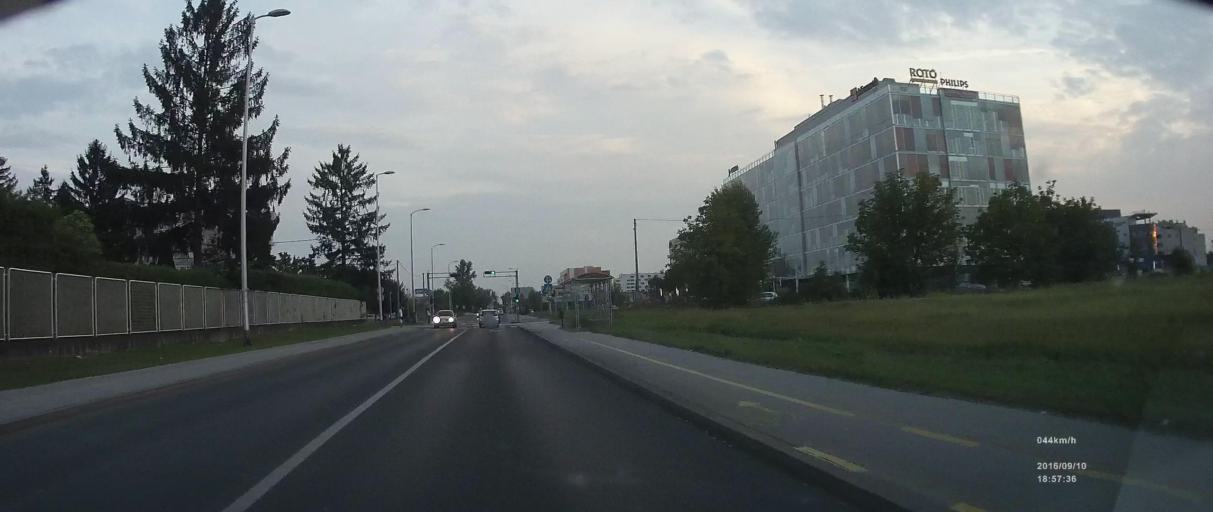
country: HR
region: Grad Zagreb
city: Novi Zagreb
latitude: 45.7654
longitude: 15.9808
